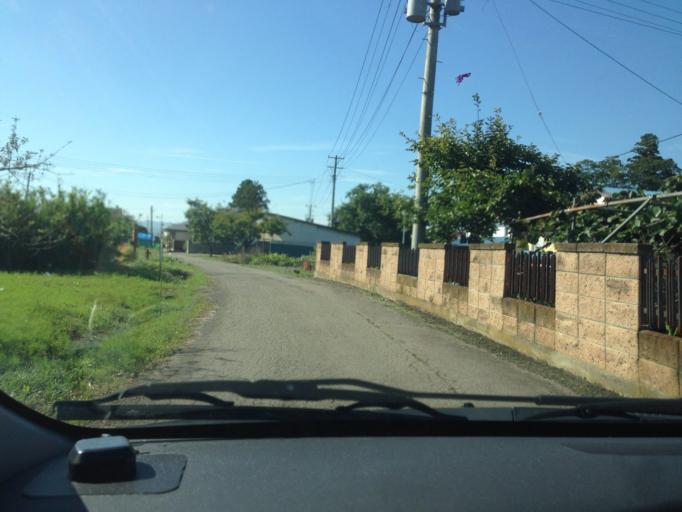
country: JP
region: Fukushima
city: Kitakata
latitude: 37.5498
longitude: 139.9167
